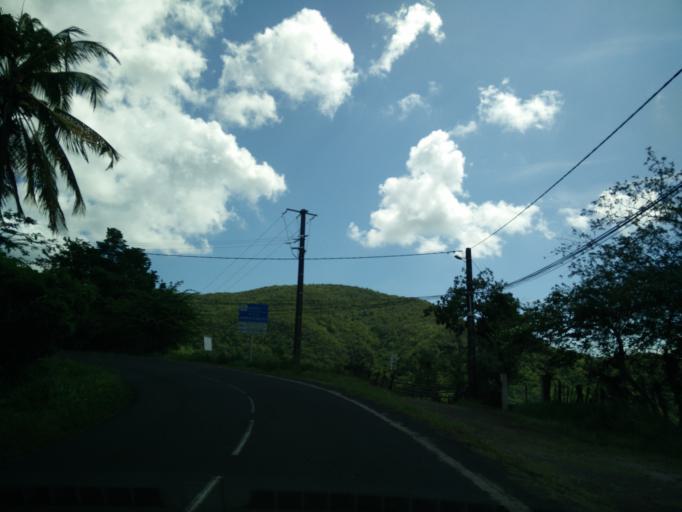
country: MQ
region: Martinique
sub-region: Martinique
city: Les Trois-Ilets
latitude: 14.5320
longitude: -61.0713
